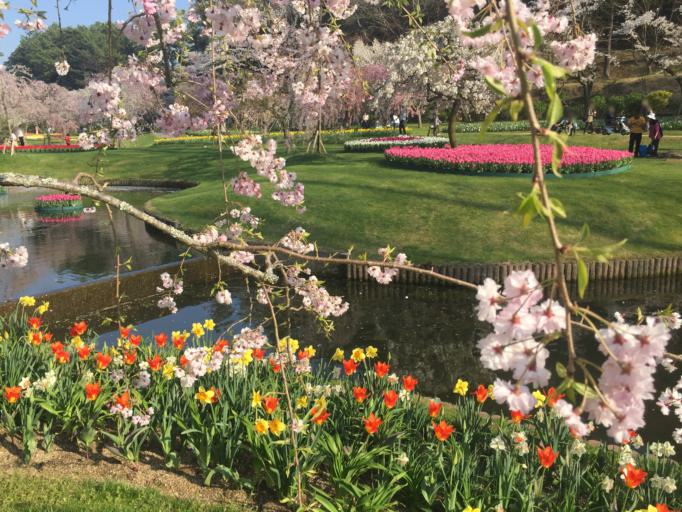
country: JP
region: Shizuoka
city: Kosai-shi
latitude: 34.7645
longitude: 137.6321
